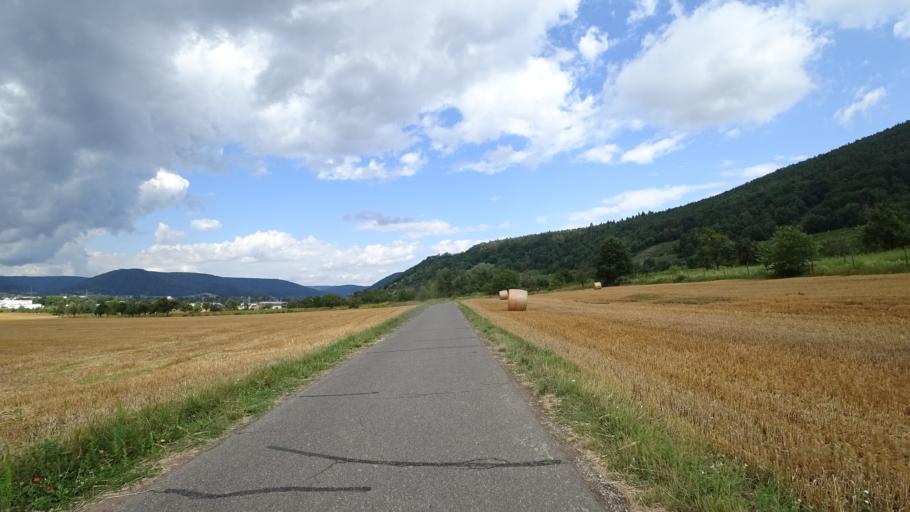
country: DE
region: Bavaria
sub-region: Regierungsbezirk Unterfranken
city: Grossheubach
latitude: 49.7171
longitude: 9.2432
